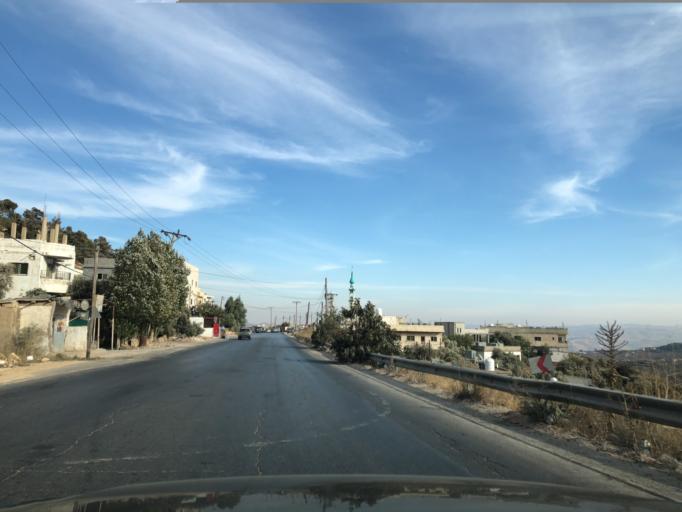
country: JO
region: Irbid
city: Sakib
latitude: 32.2849
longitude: 35.8158
